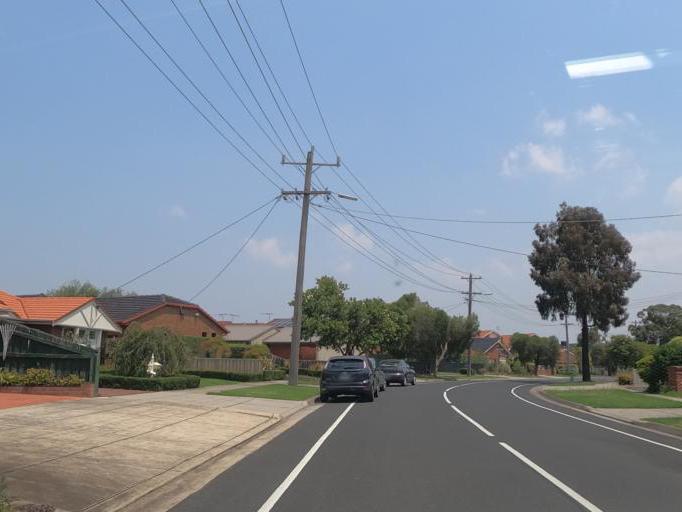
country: AU
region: Victoria
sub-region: Hume
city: Meadow Heights
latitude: -37.6441
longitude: 144.8938
